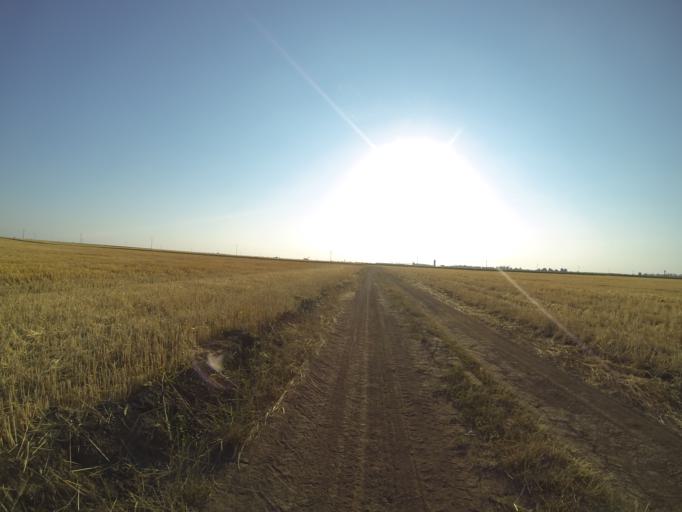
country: RO
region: Dolj
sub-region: Comuna Giurgita
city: Giurgita
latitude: 44.0299
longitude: 23.6562
